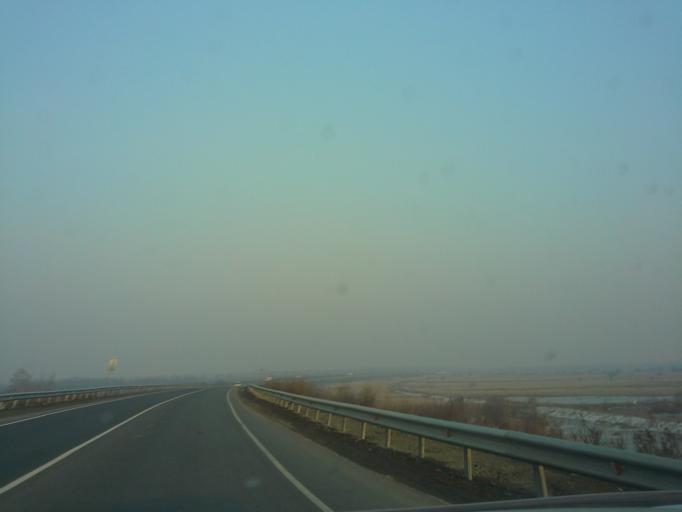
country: RU
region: Jewish Autonomous Oblast
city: Priamurskiy
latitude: 48.5223
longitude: 134.9172
